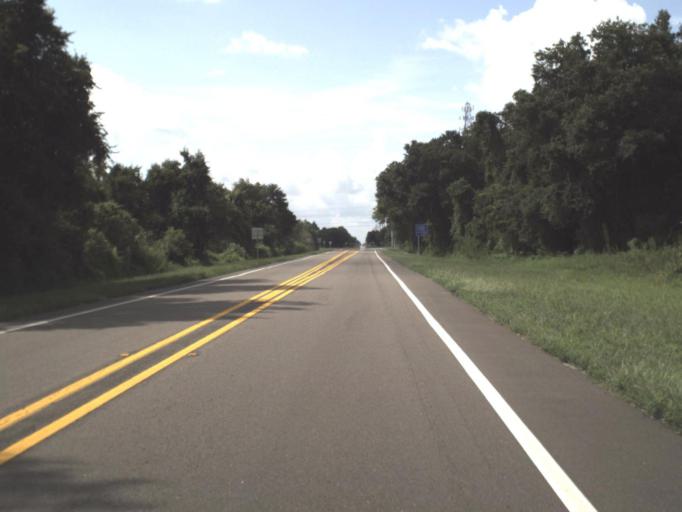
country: US
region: Florida
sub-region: Pasco County
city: Crystal Springs
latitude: 28.1752
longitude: -82.1568
